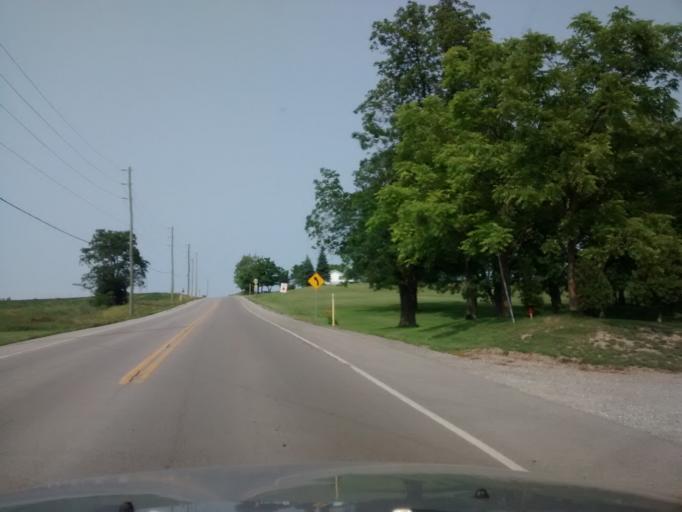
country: CA
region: Ontario
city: Ancaster
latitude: 43.0651
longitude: -79.9296
